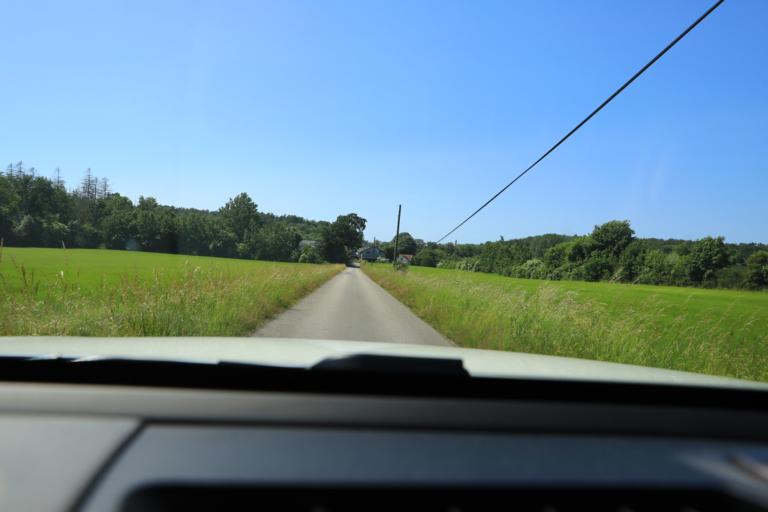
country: SE
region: Halland
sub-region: Varbergs Kommun
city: Varberg
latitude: 57.1725
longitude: 12.3049
